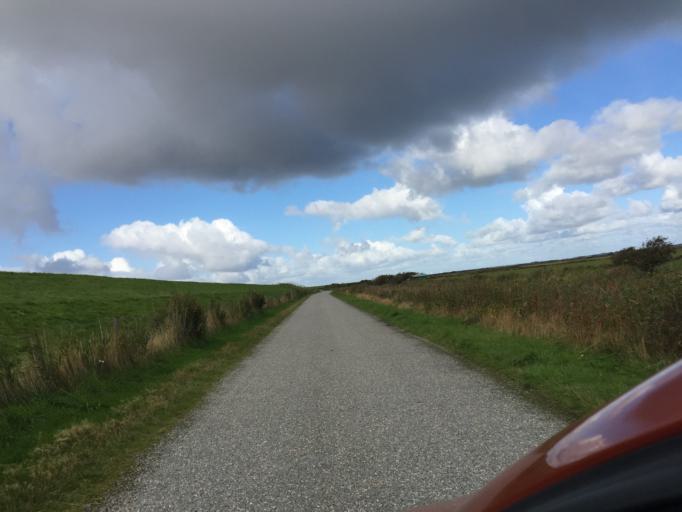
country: DK
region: South Denmark
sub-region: Esbjerg Kommune
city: Bramming
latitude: 55.3632
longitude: 8.6599
